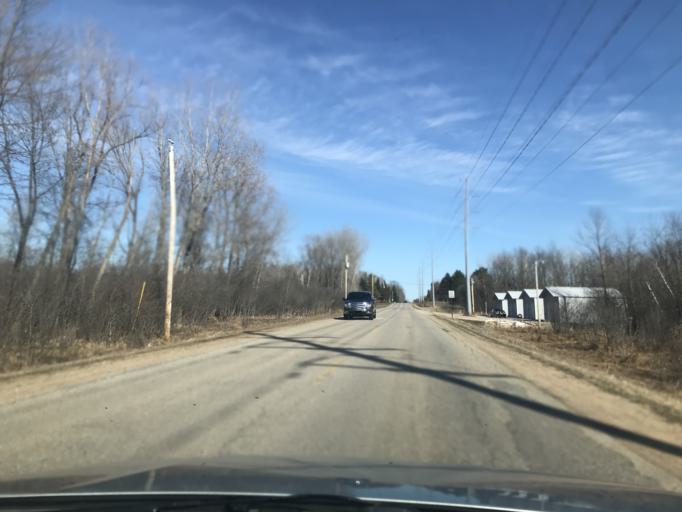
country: US
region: Wisconsin
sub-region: Marinette County
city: Marinette
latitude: 45.1450
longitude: -87.6508
